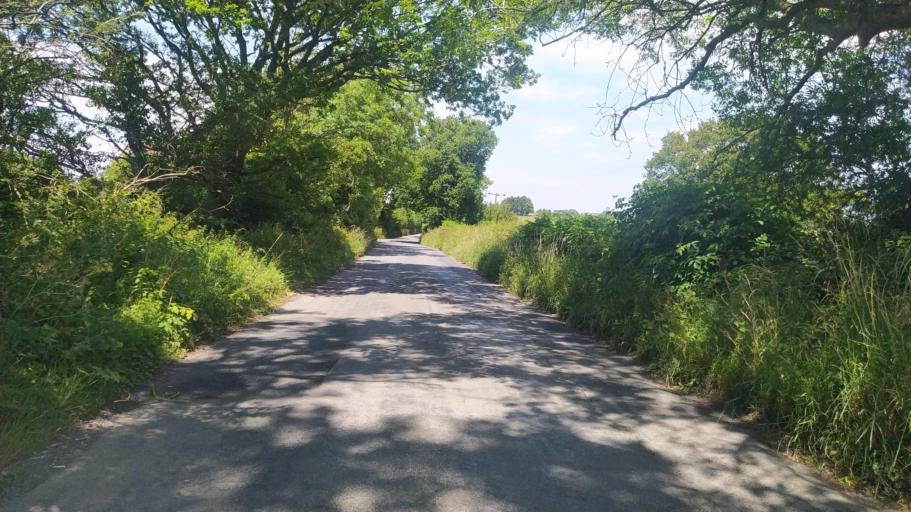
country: GB
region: England
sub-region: North Somerset
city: Banwell
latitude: 51.3339
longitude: -2.8891
